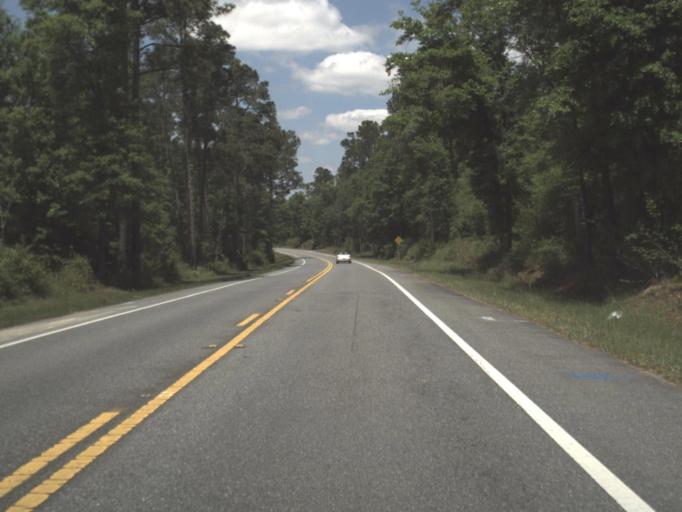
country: US
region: Florida
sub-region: Santa Rosa County
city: Point Baker
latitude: 30.7954
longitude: -87.0413
